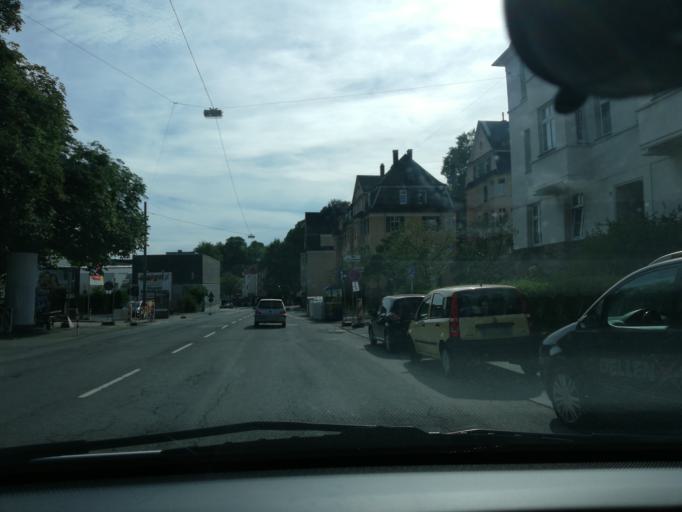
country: DE
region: North Rhine-Westphalia
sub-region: Regierungsbezirk Dusseldorf
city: Wuppertal
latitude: 51.2744
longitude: 7.1511
